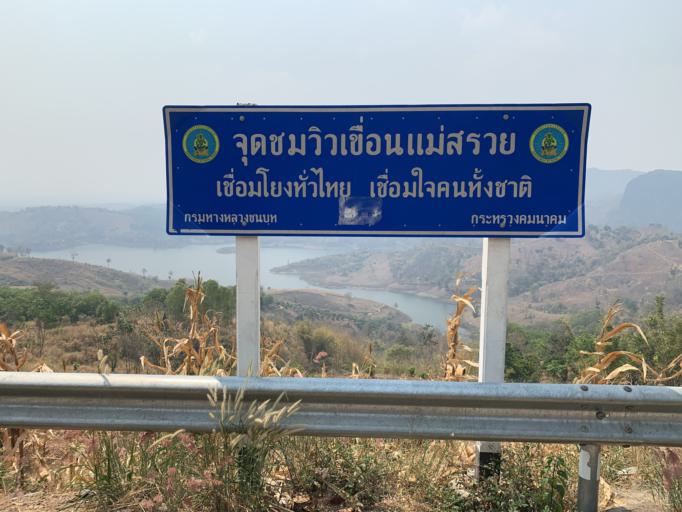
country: TH
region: Chiang Rai
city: Mae Suai
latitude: 19.6951
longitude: 99.5375
